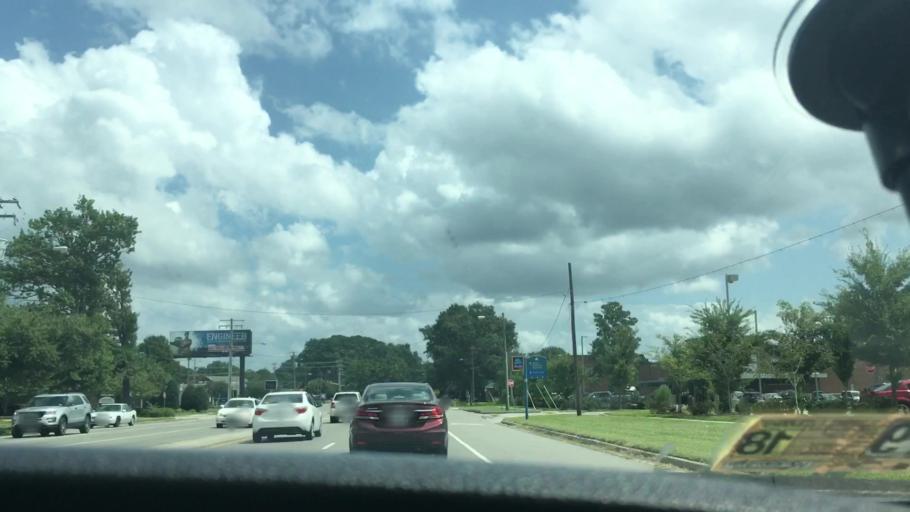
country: US
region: Virginia
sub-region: City of Portsmouth
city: Portsmouth Heights
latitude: 36.8607
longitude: -76.3953
